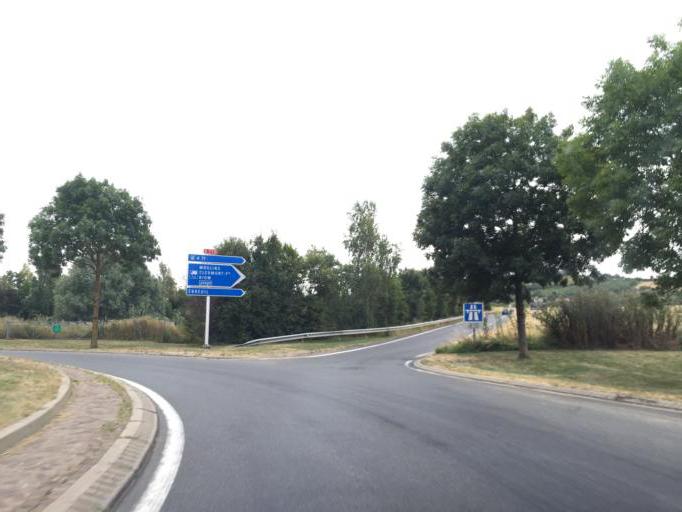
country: FR
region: Auvergne
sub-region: Departement de l'Allier
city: Gannat
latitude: 46.1154
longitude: 3.2011
